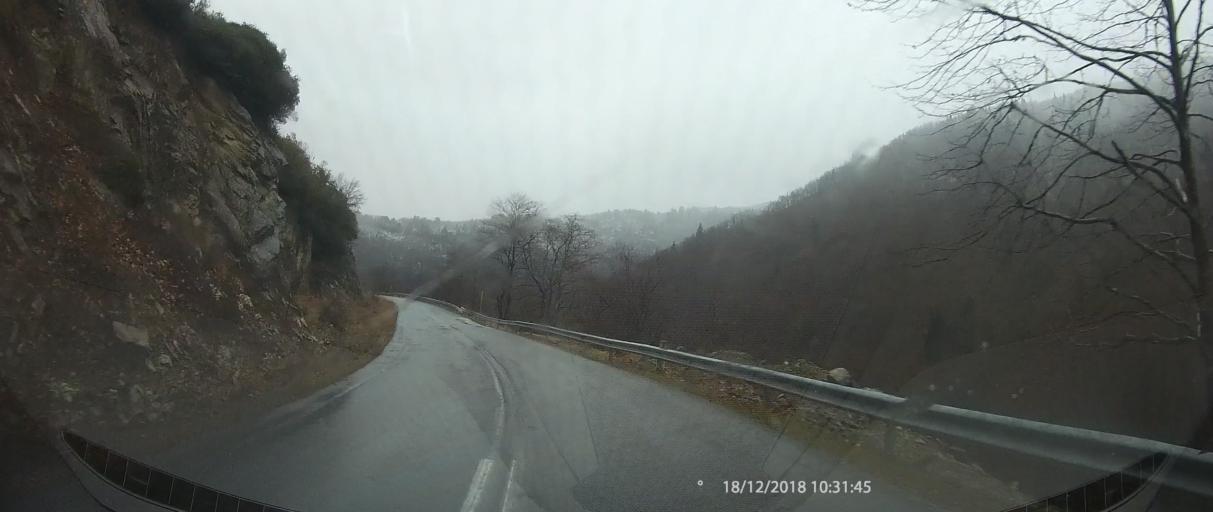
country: GR
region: Central Macedonia
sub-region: Nomos Pierias
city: Kato Milia
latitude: 40.1920
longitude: 22.2860
